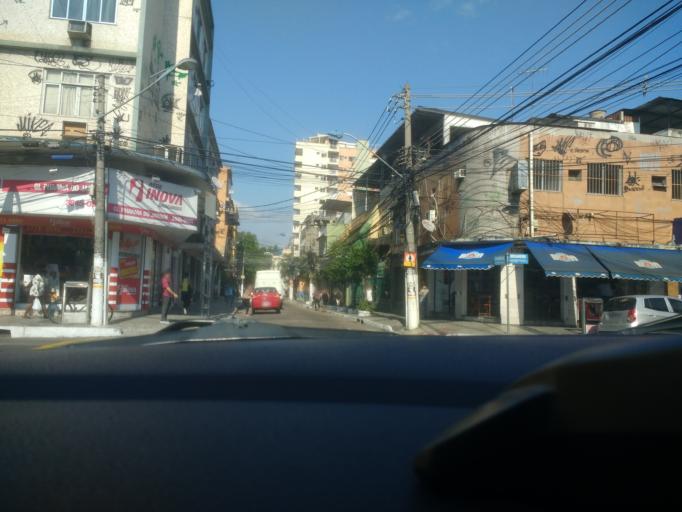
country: BR
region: Rio de Janeiro
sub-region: Duque De Caxias
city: Duque de Caxias
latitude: -22.7923
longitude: -43.3019
